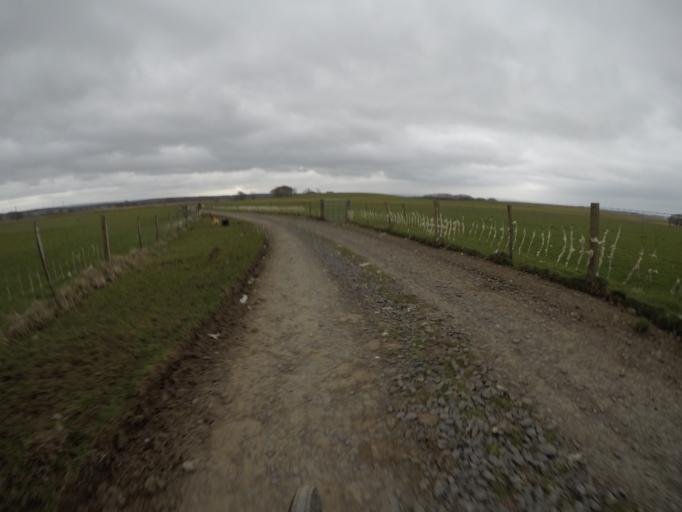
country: GB
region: Scotland
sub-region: East Ayrshire
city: Galston
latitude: 55.6718
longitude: -4.3733
